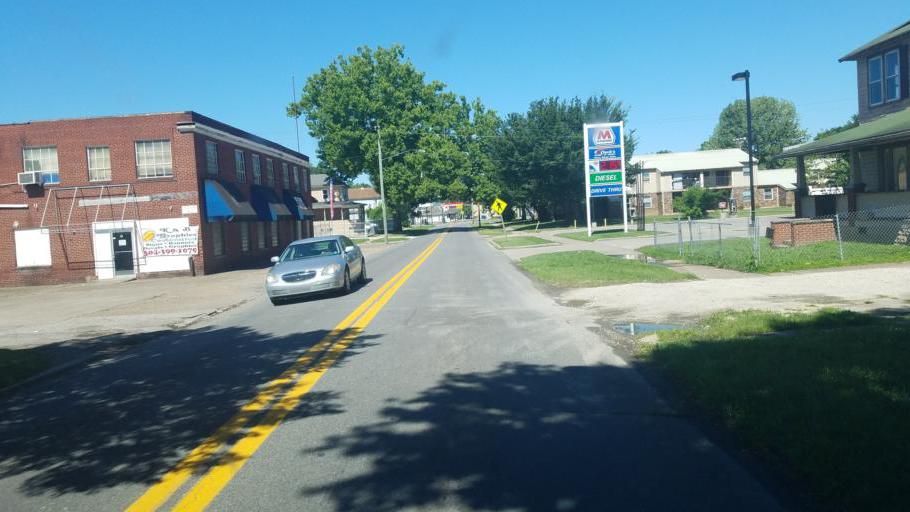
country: US
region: West Virginia
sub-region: Cabell County
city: Huntington
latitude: 38.4293
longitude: -82.3826
